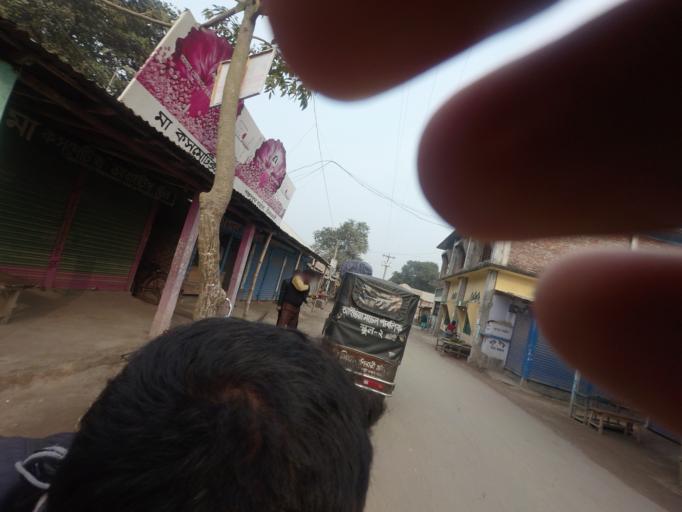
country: BD
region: Rajshahi
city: Saidpur
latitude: 25.9294
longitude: 88.9290
